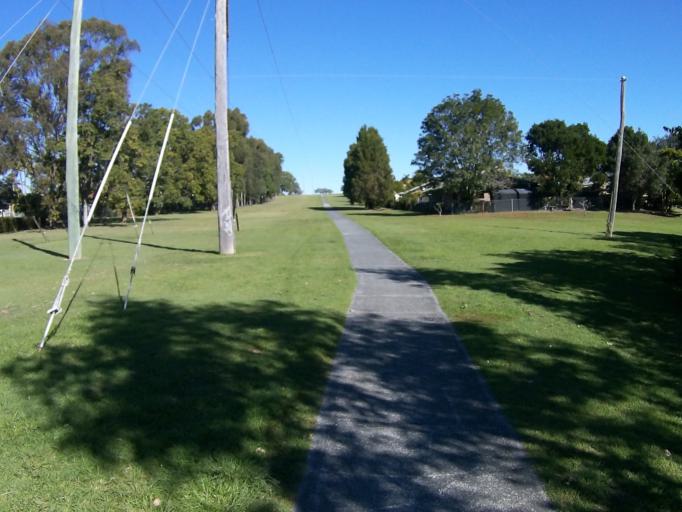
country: AU
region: Queensland
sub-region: Logan
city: Windaroo
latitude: -27.7388
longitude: 153.1940
